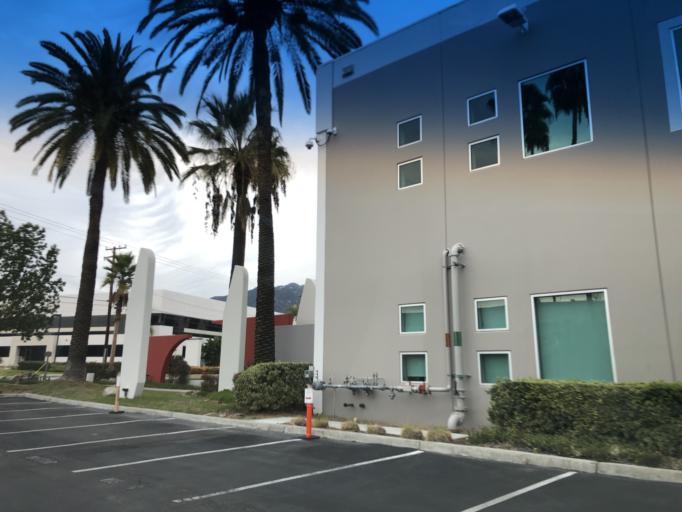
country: US
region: California
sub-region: Los Angeles County
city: Arcadia
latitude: 34.1379
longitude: -118.0201
